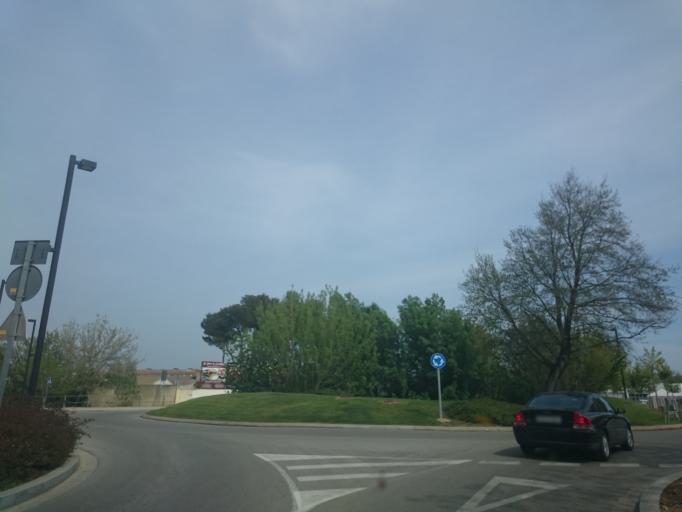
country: ES
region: Catalonia
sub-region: Provincia de Girona
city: Figueres
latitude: 42.2667
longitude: 2.9768
